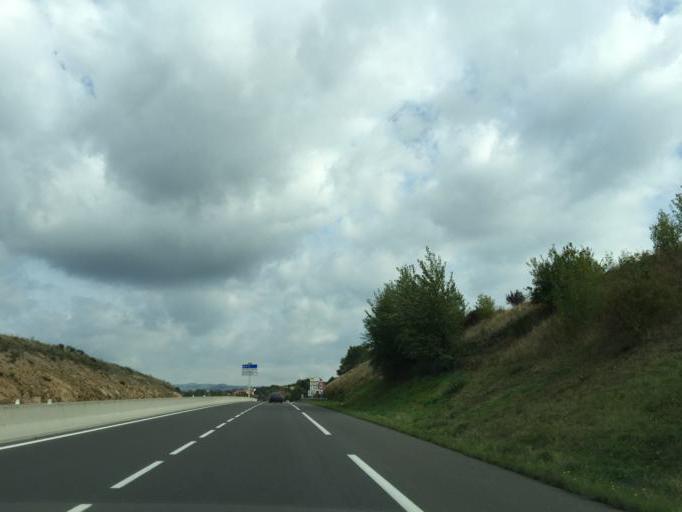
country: FR
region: Rhone-Alpes
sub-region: Departement de la Loire
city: Andrezieux-Boutheon
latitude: 45.5173
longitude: 4.2586
